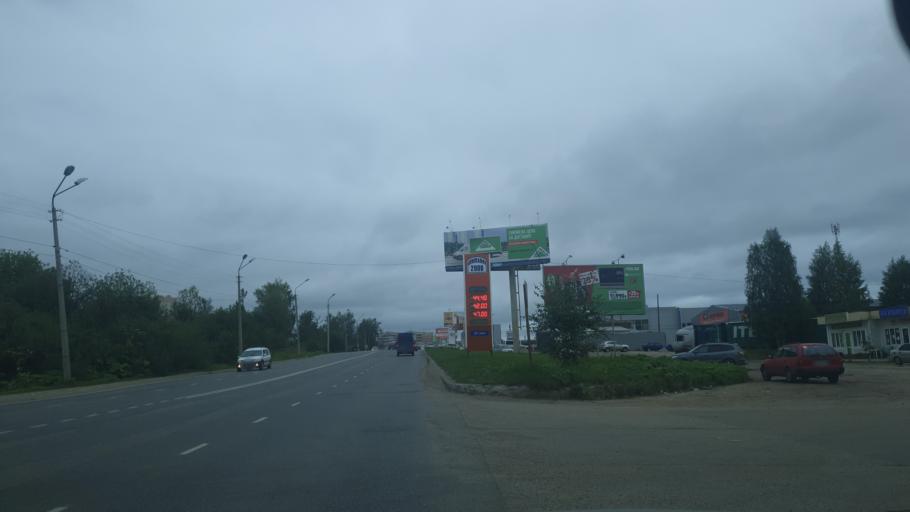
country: RU
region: Komi Republic
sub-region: Syktyvdinskiy Rayon
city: Syktyvkar
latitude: 61.6363
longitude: 50.8125
